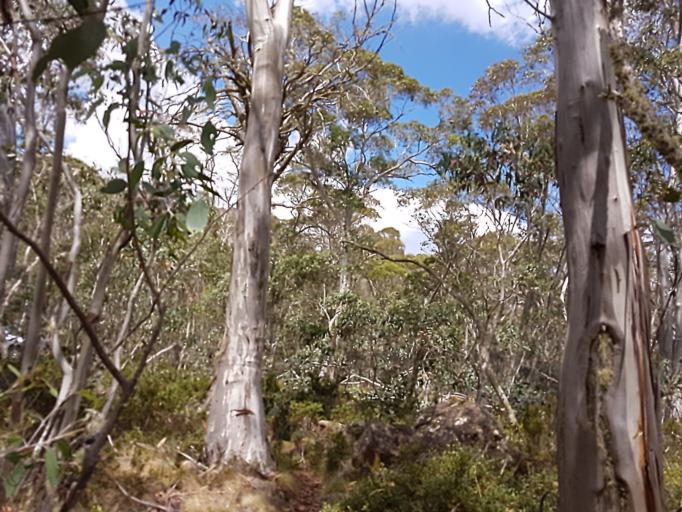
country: AU
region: New South Wales
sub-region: Snowy River
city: Jindabyne
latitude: -36.9016
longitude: 148.1195
